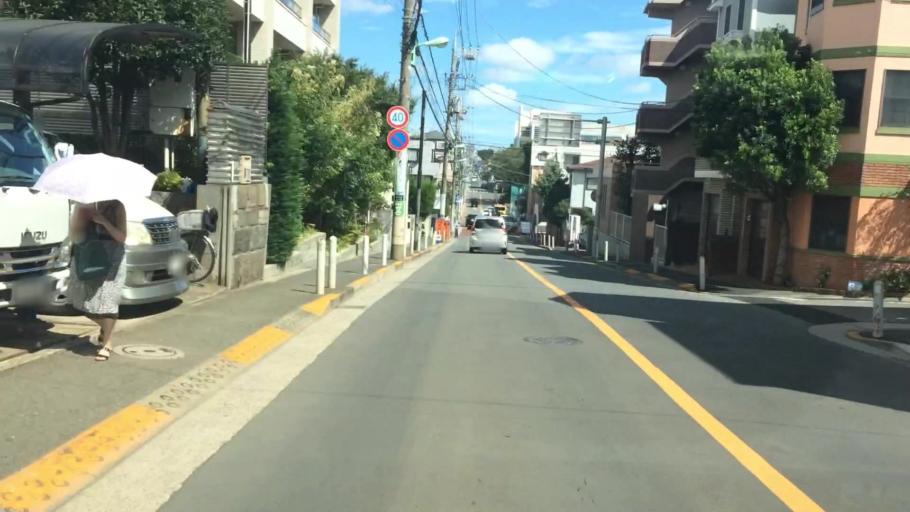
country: JP
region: Tokyo
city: Tokyo
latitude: 35.6142
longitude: 139.6489
